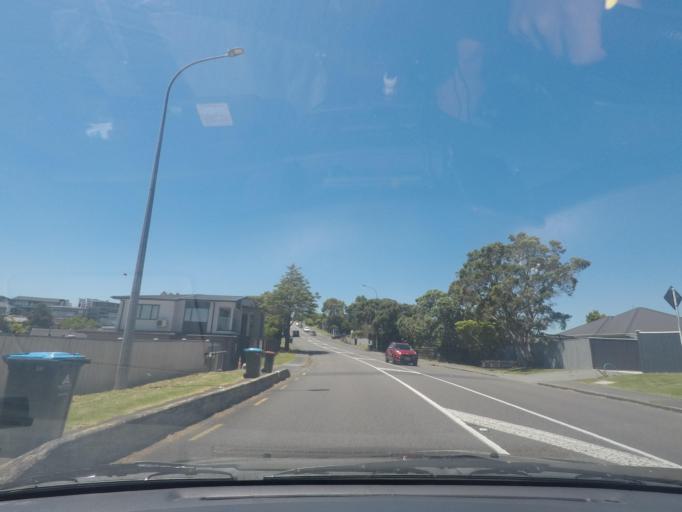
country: NZ
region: Auckland
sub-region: Auckland
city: Mangere
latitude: -36.9285
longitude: 174.7476
